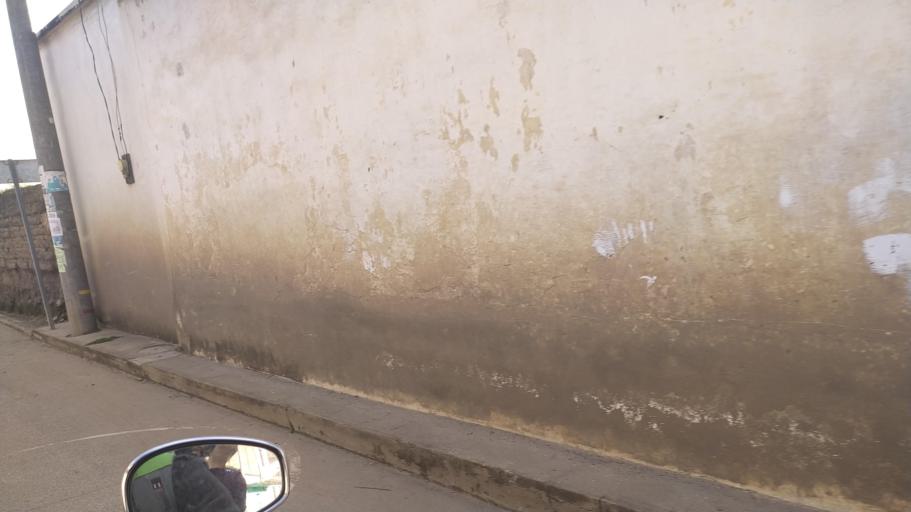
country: GT
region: Quetzaltenango
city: Salcaja
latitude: 14.8721
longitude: -91.4590
